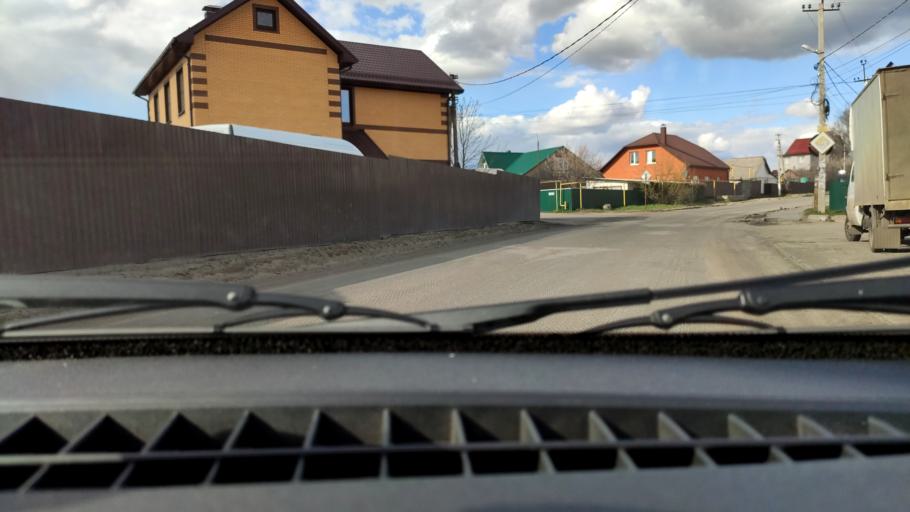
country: RU
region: Voronezj
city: Podgornoye
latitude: 51.7356
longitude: 39.1583
